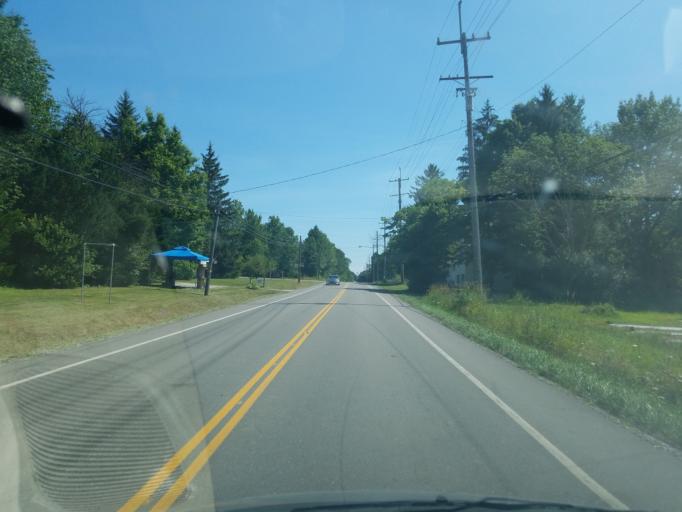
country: US
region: Ohio
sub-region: Geauga County
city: Burton
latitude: 41.4981
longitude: -81.1453
